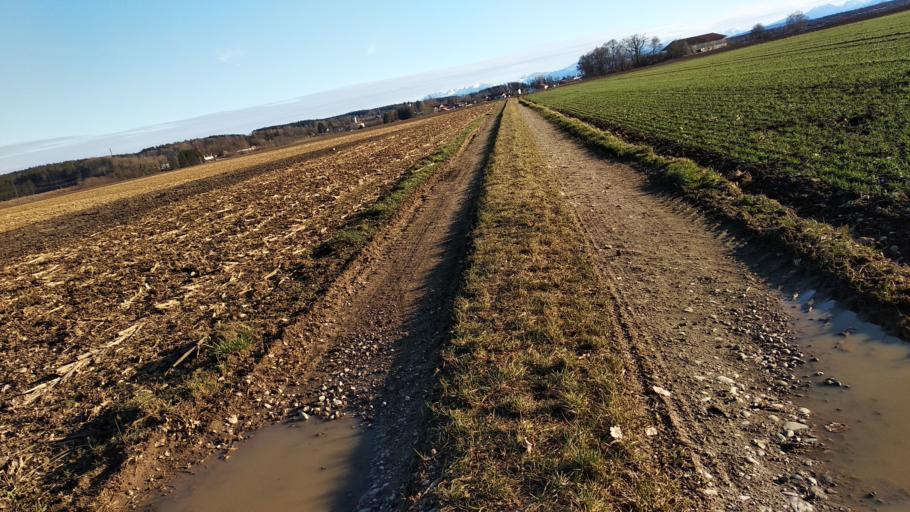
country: DE
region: Bavaria
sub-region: Upper Bavaria
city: Aying
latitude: 47.9843
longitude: 11.7715
